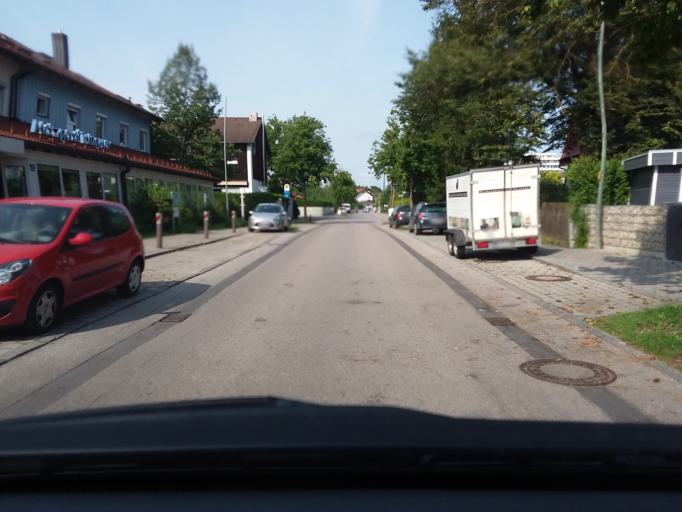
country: DE
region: Bavaria
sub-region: Upper Bavaria
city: Oberschleissheim
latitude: 48.2526
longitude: 11.5480
